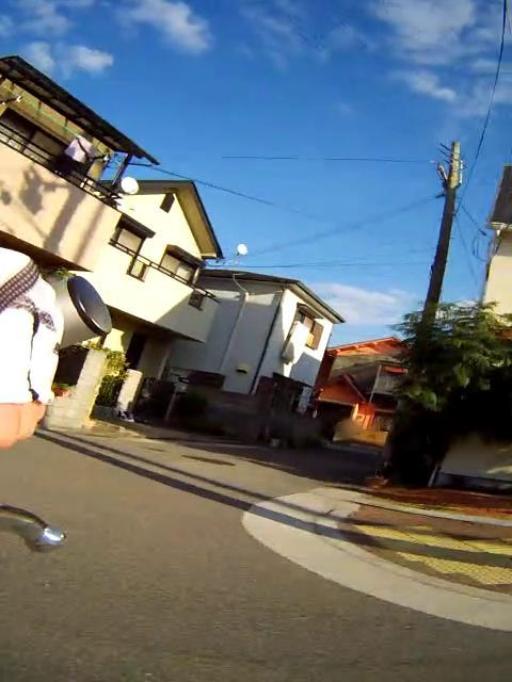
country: JP
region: Hyogo
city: Takarazuka
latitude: 34.7666
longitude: 135.3693
